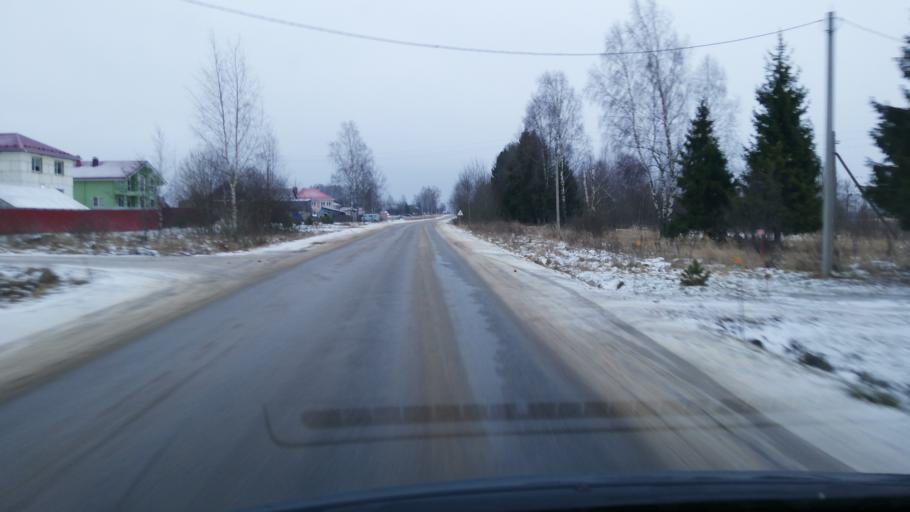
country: RU
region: Kostroma
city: Oktyabr'skiy
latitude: 57.7166
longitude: 41.1413
